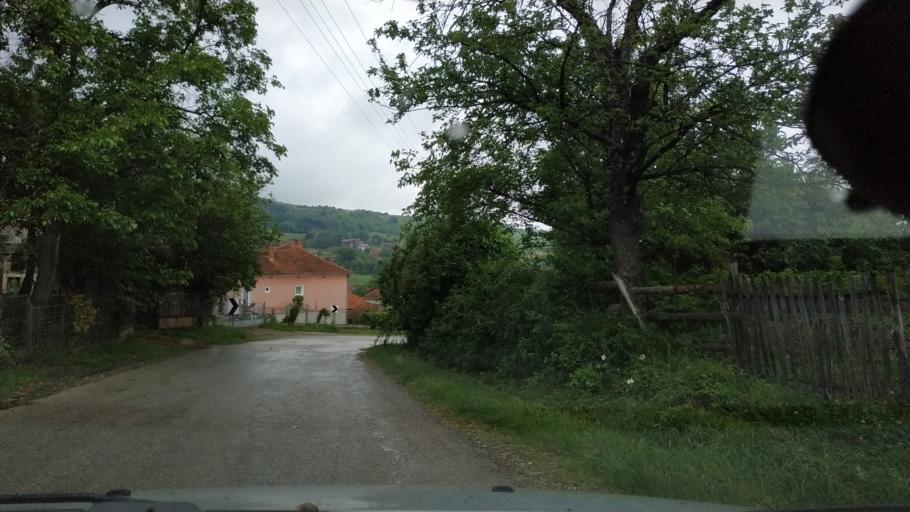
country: RS
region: Central Serbia
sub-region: Toplicki Okrug
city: Prokuplje
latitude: 43.3962
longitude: 21.5547
